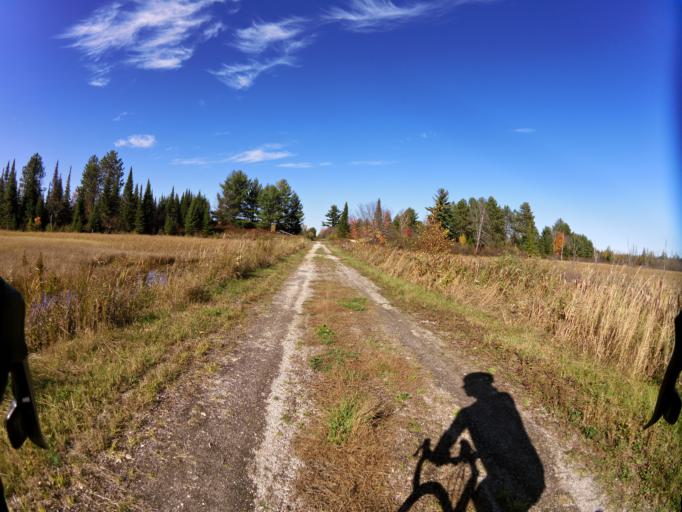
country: CA
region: Quebec
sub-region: Outaouais
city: Wakefield
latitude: 45.9082
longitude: -76.0414
